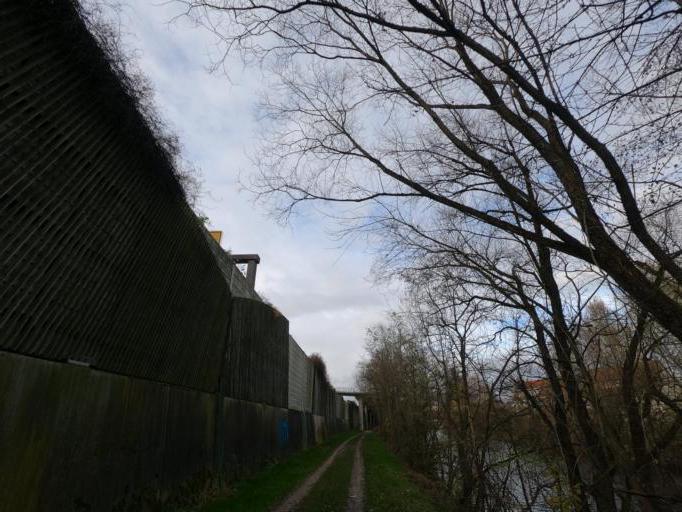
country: DE
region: Baden-Wuerttemberg
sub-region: Regierungsbezirk Stuttgart
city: Uhingen
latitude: 48.7041
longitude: 9.5811
